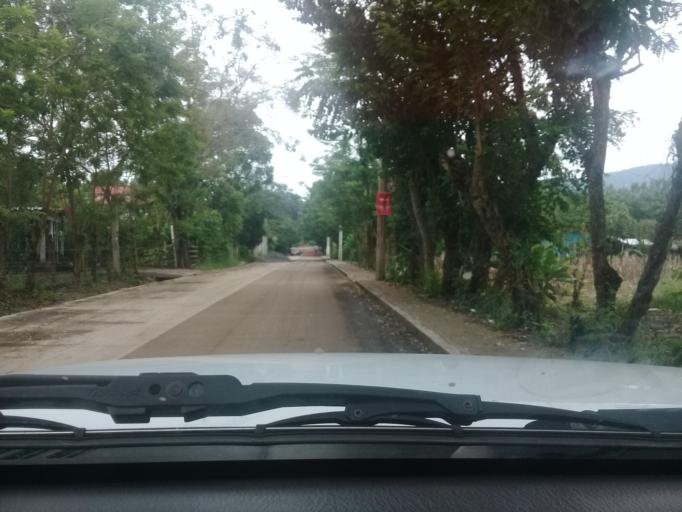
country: MX
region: Veracruz
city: Comoapan
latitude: 18.4105
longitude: -95.1782
